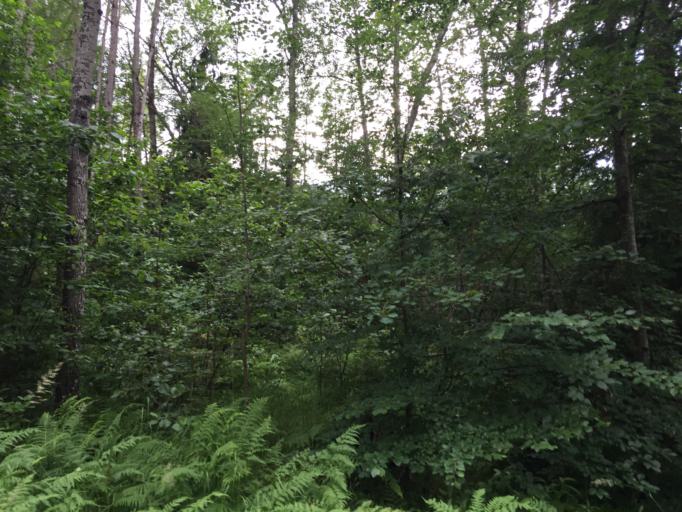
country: SE
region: Stockholm
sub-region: Salems Kommun
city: Ronninge
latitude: 59.1887
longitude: 17.7620
